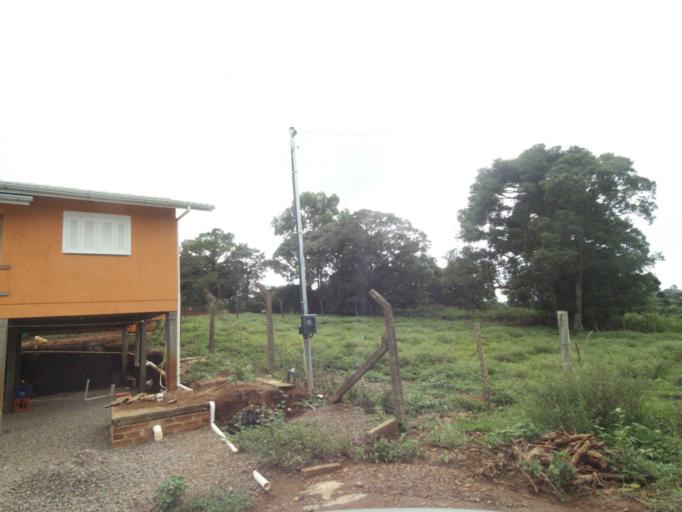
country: BR
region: Rio Grande do Sul
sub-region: Lagoa Vermelha
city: Lagoa Vermelha
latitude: -28.2313
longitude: -51.5075
